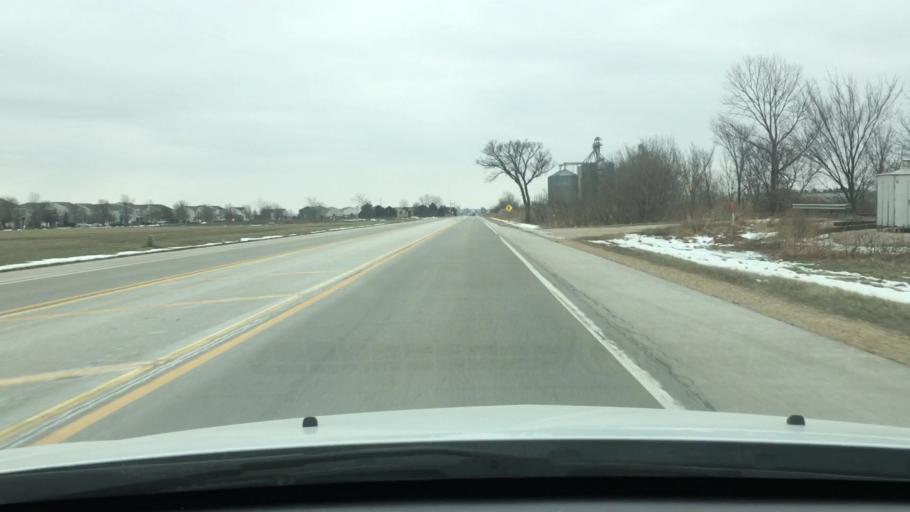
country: US
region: Illinois
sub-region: DeKalb County
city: Waterman
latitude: 41.7691
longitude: -88.7658
